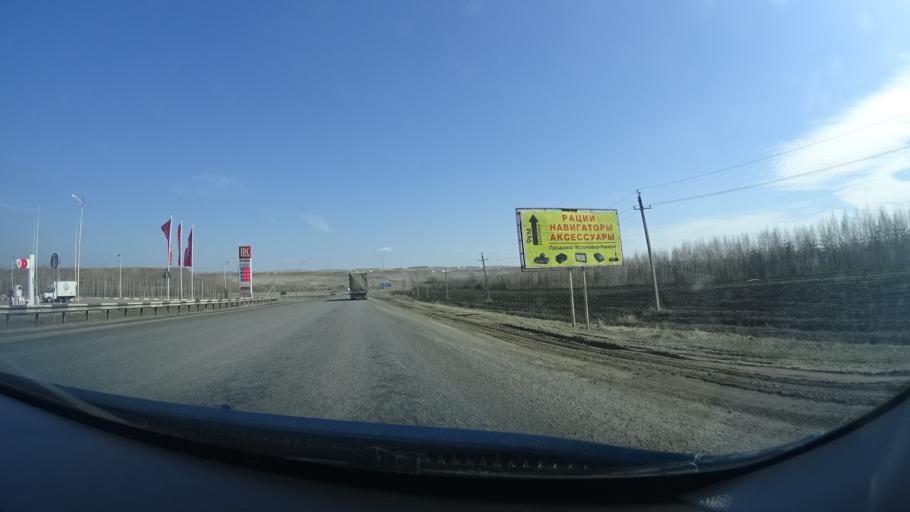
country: RU
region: Bashkortostan
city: Subkhankulovo
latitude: 54.4853
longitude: 53.8998
